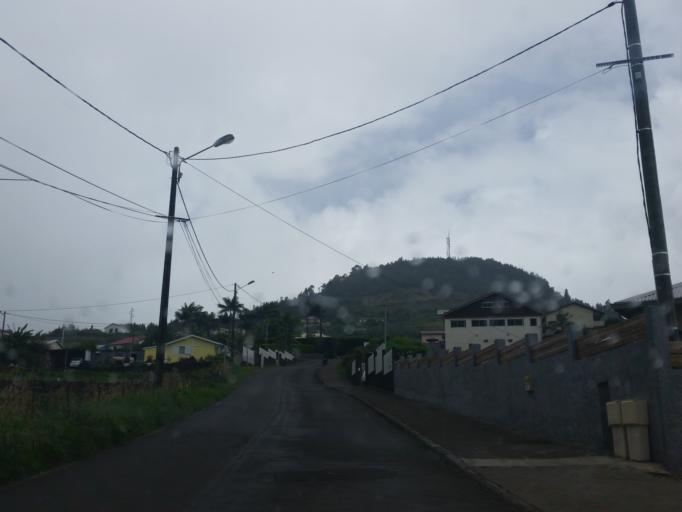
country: RE
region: Reunion
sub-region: Reunion
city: Le Tampon
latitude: -21.2223
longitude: 55.5317
